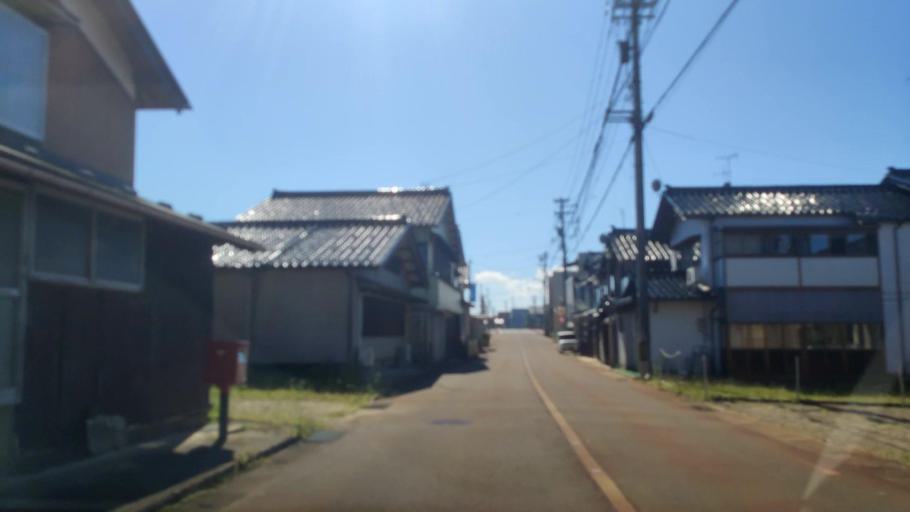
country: JP
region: Ishikawa
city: Nanao
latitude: 37.4380
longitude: 137.2677
